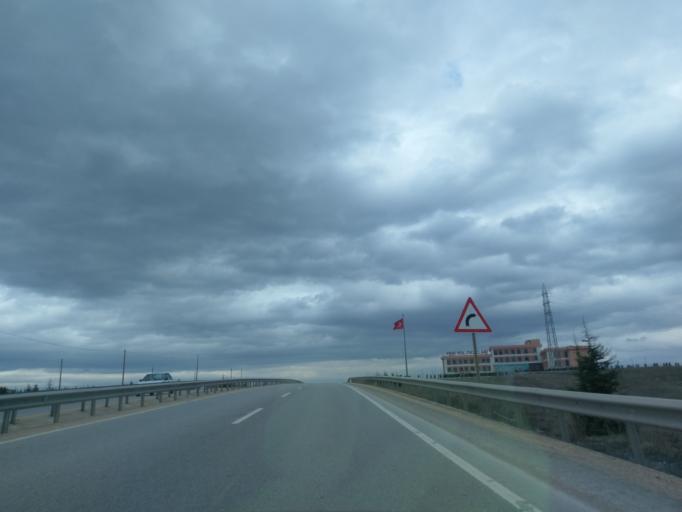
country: TR
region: Eskisehir
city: Eskisehir
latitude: 39.7395
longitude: 30.3919
